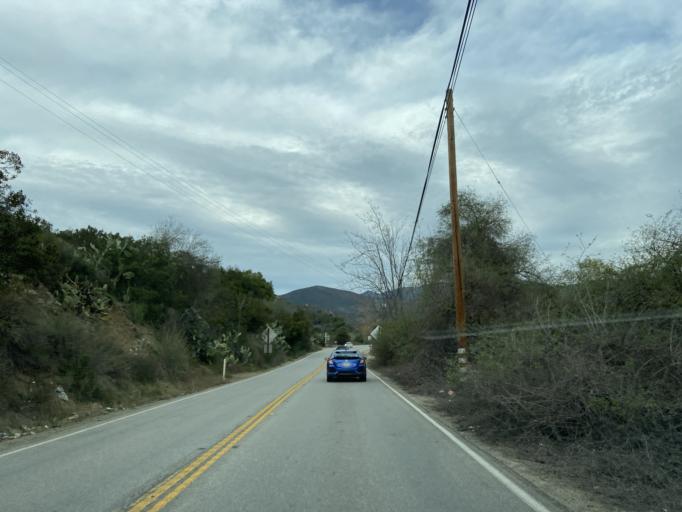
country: US
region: California
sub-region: San Diego County
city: Rainbow
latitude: 33.3630
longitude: -117.1014
